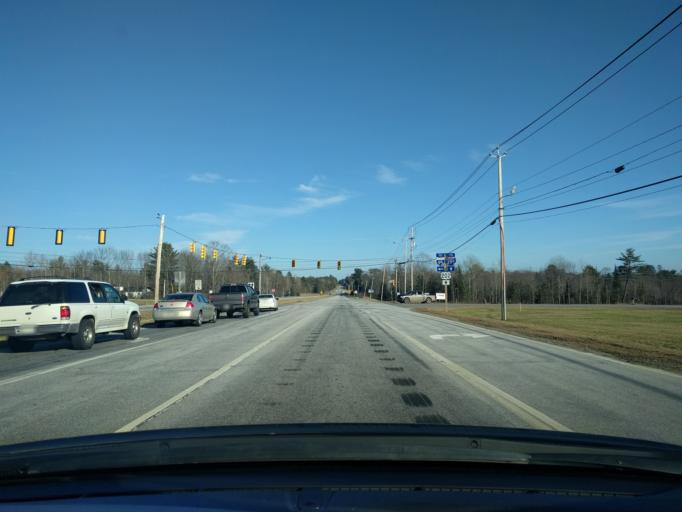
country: US
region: Maine
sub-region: Penobscot County
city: Hampden
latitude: 44.7538
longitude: -68.8400
